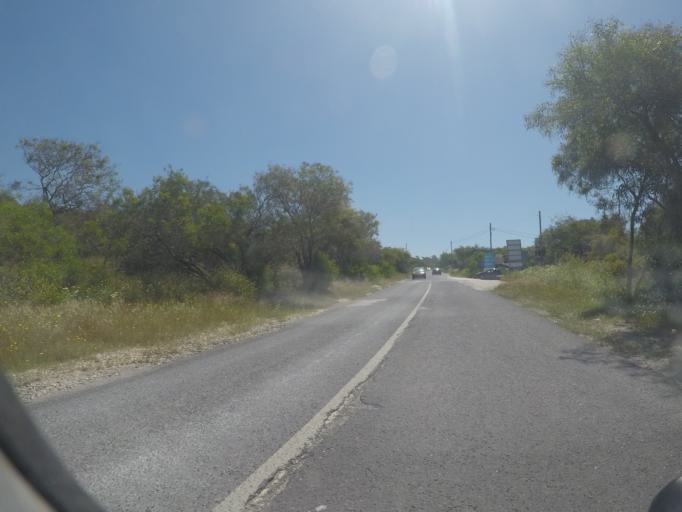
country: PT
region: Setubal
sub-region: Almada
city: Charneca
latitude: 38.6097
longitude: -9.2065
